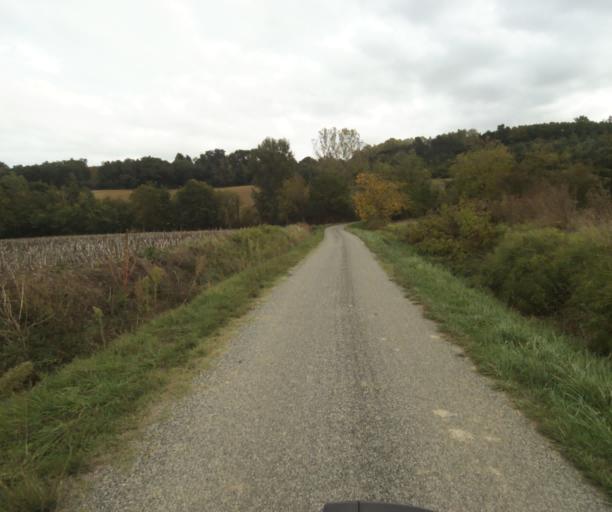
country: FR
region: Midi-Pyrenees
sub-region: Departement du Tarn-et-Garonne
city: Verdun-sur-Garonne
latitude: 43.8464
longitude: 1.1169
